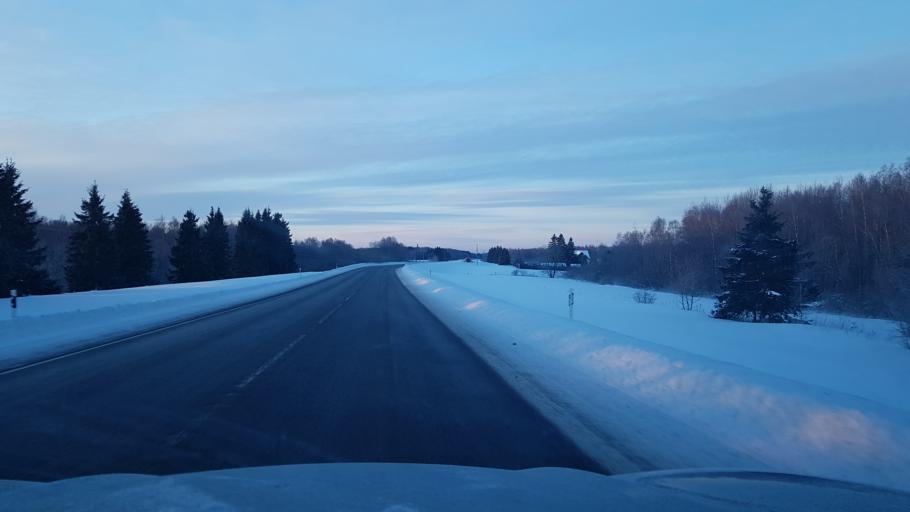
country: EE
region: Ida-Virumaa
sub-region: Narva-Joesuu linn
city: Narva-Joesuu
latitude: 59.3868
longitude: 27.9742
